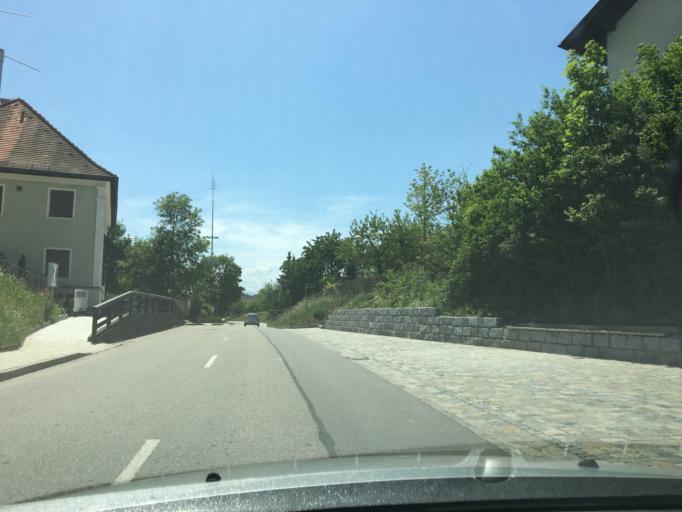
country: DE
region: Bavaria
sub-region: Upper Bavaria
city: Halsbach
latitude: 48.0988
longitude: 12.7246
